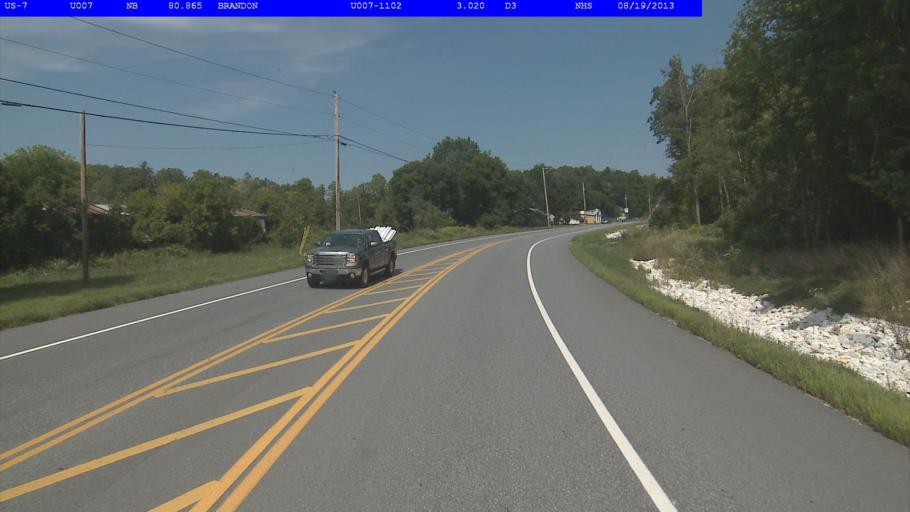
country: US
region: Vermont
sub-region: Rutland County
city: Brandon
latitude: 43.7886
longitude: -73.0767
